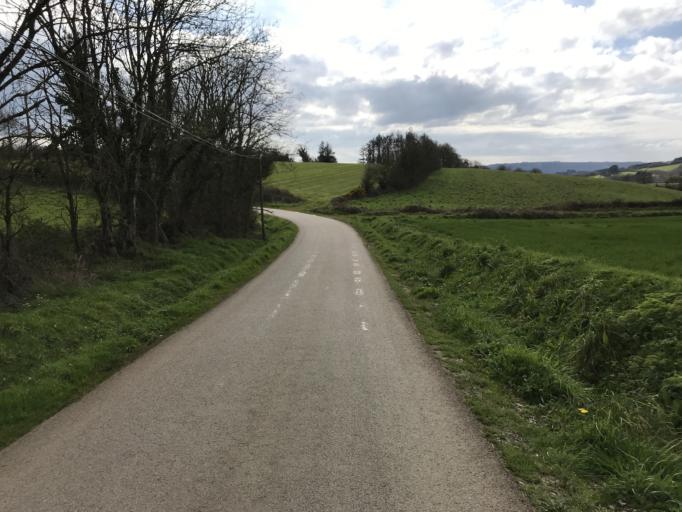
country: FR
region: Brittany
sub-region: Departement du Finistere
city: Hopital-Camfrout
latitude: 48.3195
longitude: -4.2142
